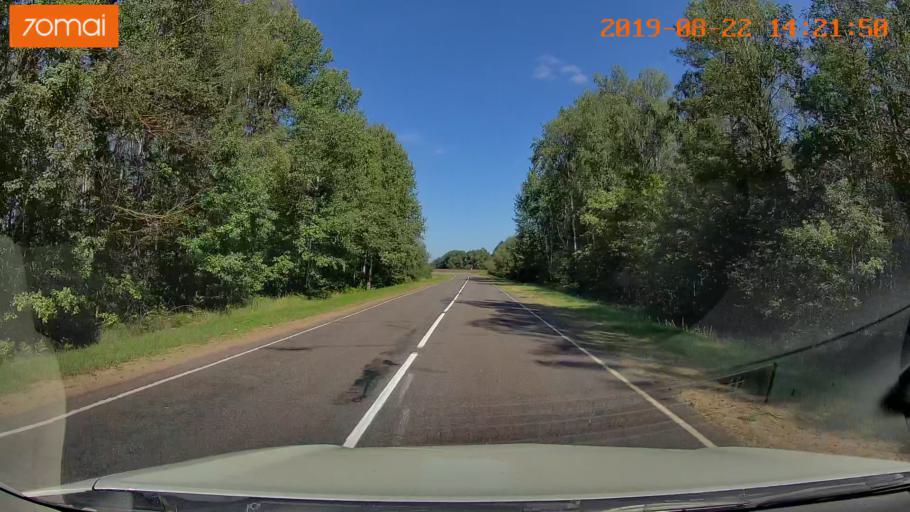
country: BY
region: Mogilev
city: Asipovichy
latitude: 53.2696
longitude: 28.5648
